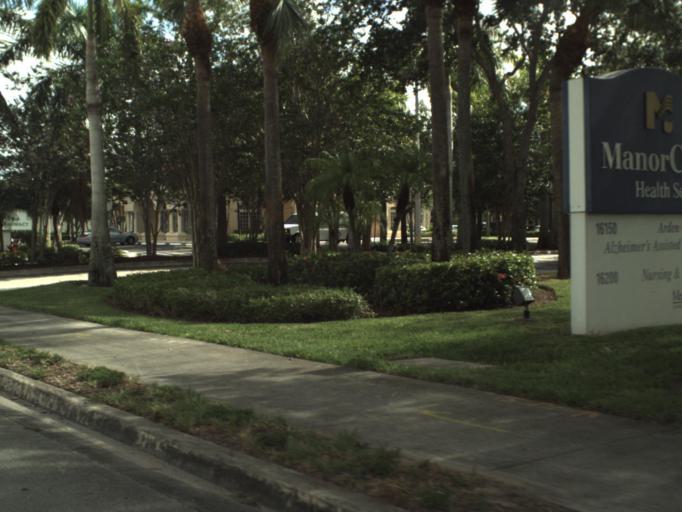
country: US
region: Florida
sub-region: Palm Beach County
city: Kings Point
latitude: 26.4369
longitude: -80.1464
